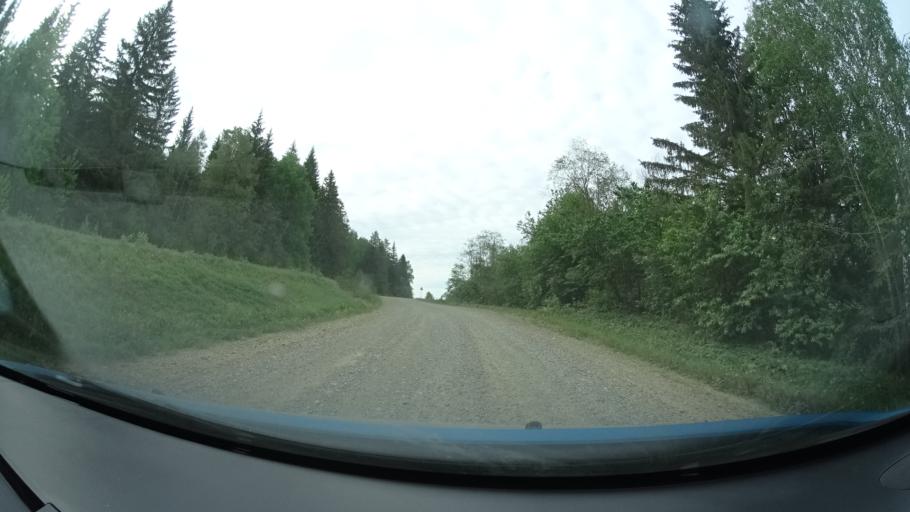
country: RU
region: Perm
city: Kuyeda
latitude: 56.6559
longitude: 55.6921
